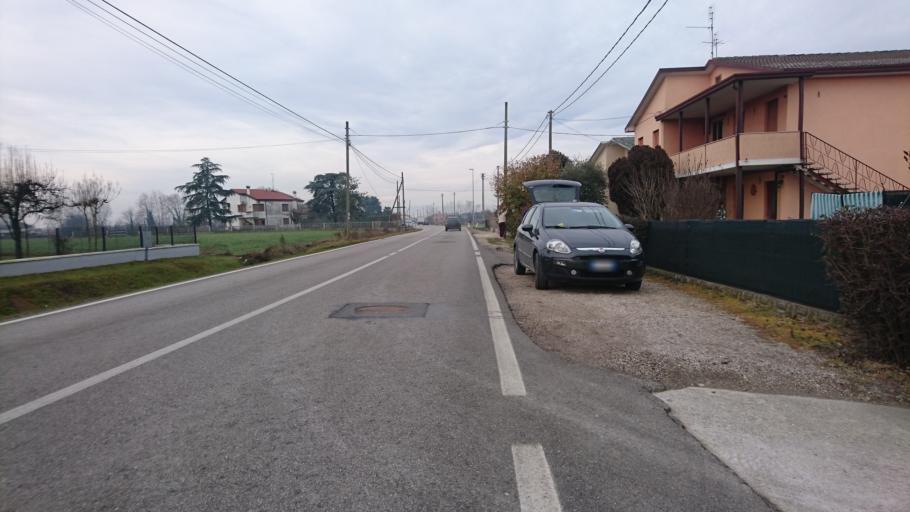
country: IT
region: Veneto
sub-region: Provincia di Padova
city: Ronchi di Campanile
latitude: 45.4709
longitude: 11.7890
